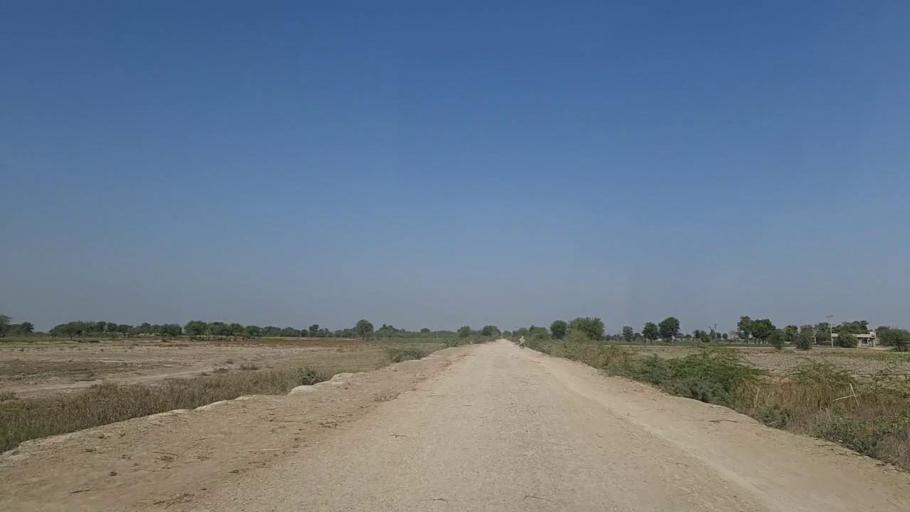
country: PK
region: Sindh
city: Samaro
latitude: 25.1759
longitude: 69.4040
